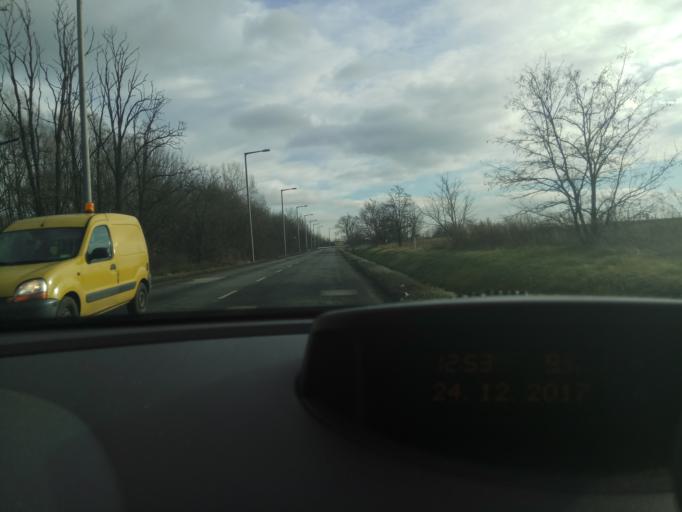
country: HU
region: Budapest
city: Budapest XV. keruelet
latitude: 47.5797
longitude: 19.1416
